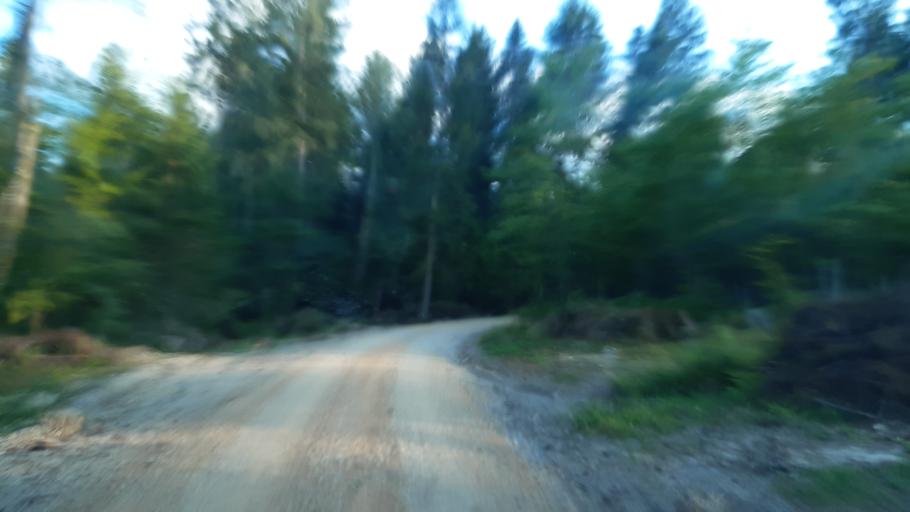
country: SI
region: Dolenjske Toplice
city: Dolenjske Toplice
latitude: 45.6945
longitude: 15.0110
